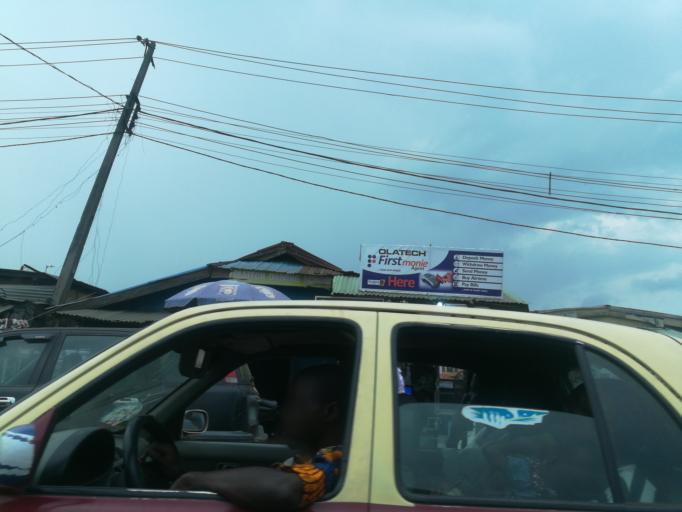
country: NG
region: Oyo
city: Moniya
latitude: 7.4670
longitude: 3.9125
